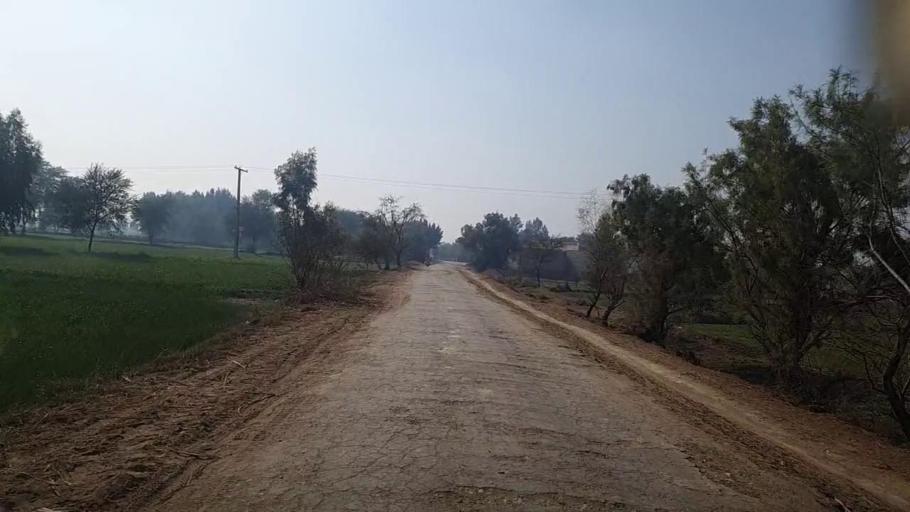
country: PK
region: Sindh
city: Khairpur
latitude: 27.9415
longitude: 69.6714
